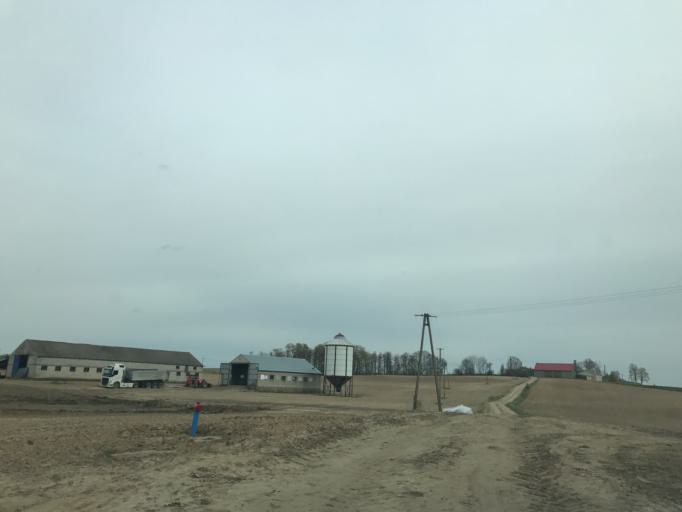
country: PL
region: Warmian-Masurian Voivodeship
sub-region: Powiat ilawski
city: Lubawa
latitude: 53.4360
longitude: 19.8237
